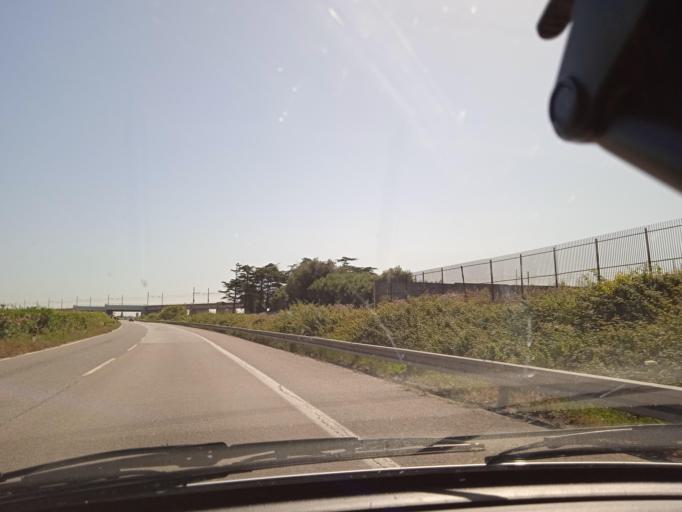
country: IT
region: Sicily
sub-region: Messina
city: Barcellona Pozzo di Gotto
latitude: 38.1647
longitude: 15.2110
